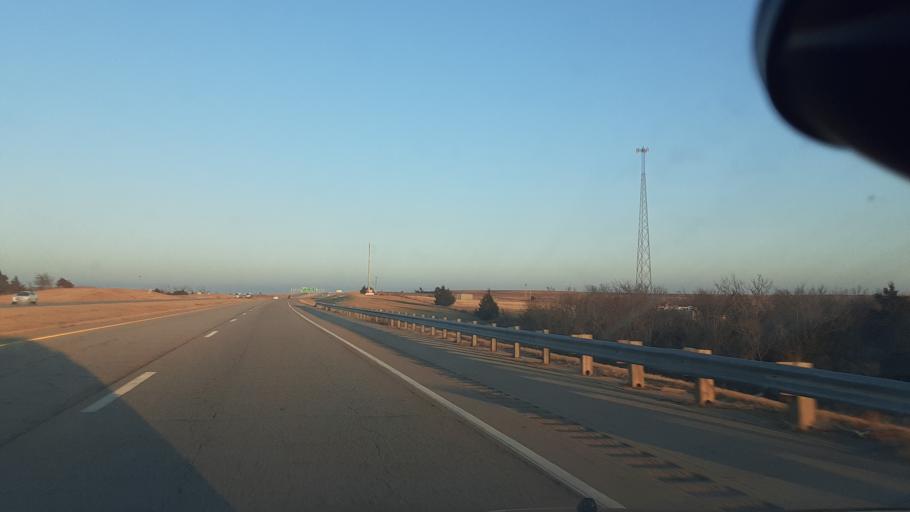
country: US
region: Oklahoma
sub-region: Noble County
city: Perry
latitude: 36.3996
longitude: -97.3408
